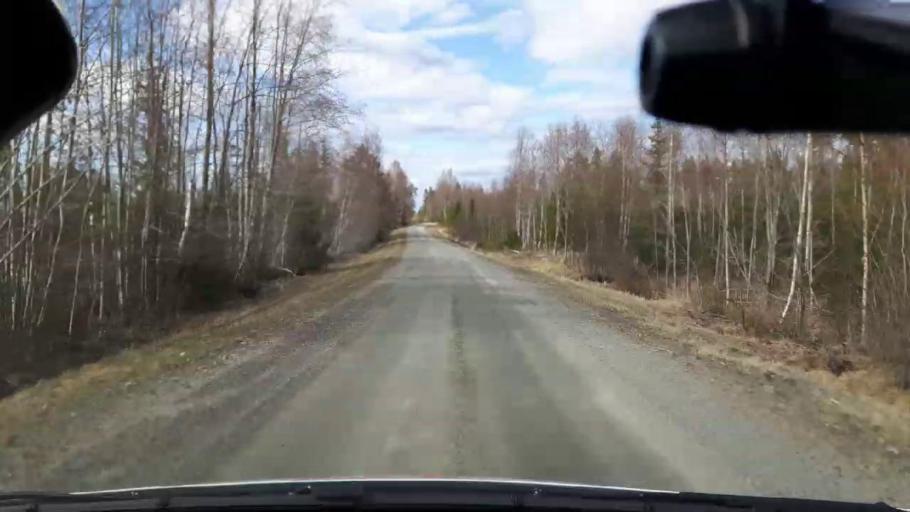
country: SE
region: Jaemtland
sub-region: Bergs Kommun
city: Hoverberg
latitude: 62.7497
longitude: 14.6633
